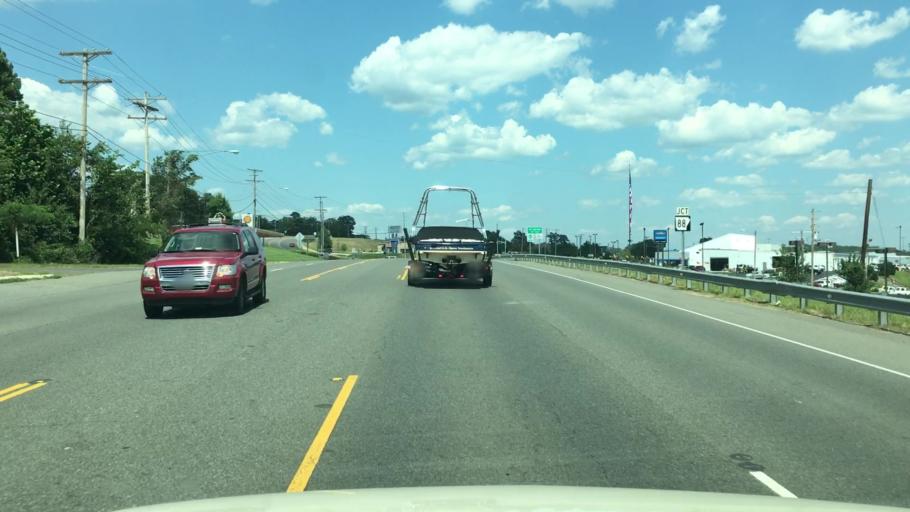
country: US
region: Arkansas
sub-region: Garland County
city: Lake Hamilton
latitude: 34.4474
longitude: -93.0880
